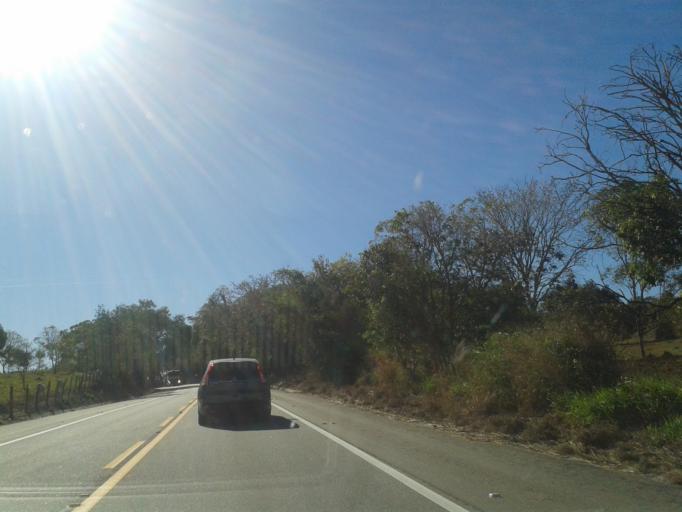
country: BR
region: Goias
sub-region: Itapuranga
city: Itapuranga
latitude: -15.5888
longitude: -50.2608
